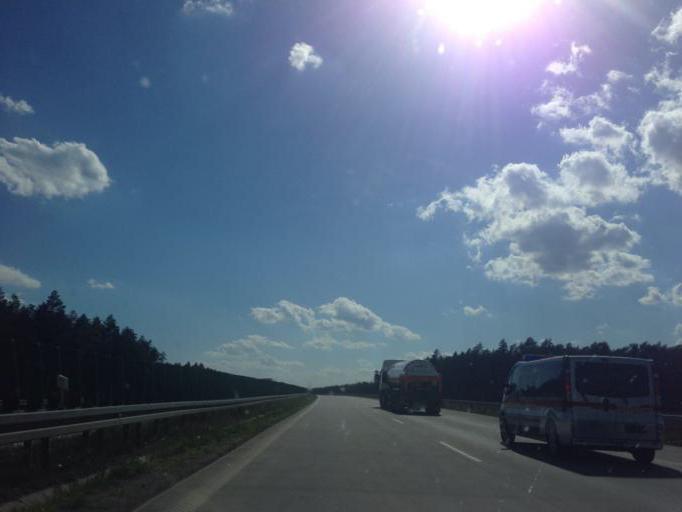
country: PL
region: Lower Silesian Voivodeship
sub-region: Powiat boleslawiecki
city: Boleslawiec
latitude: 51.3033
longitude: 15.5139
